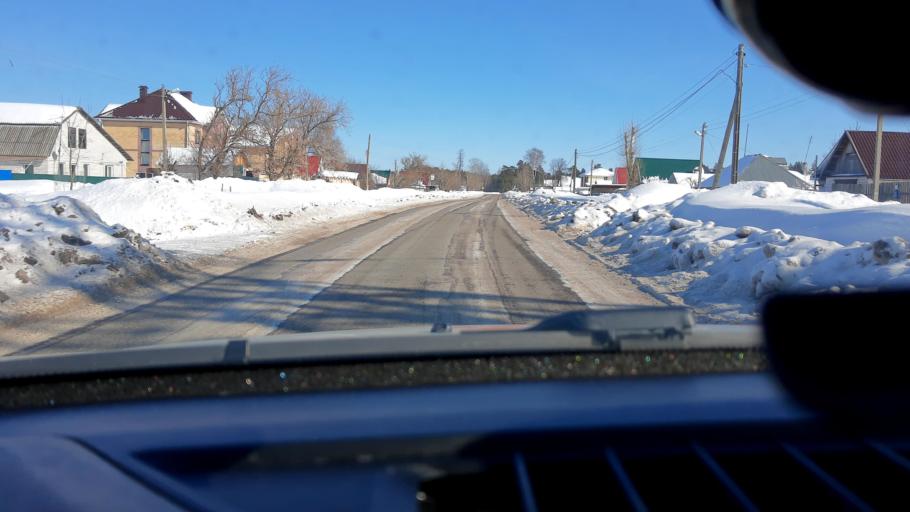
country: RU
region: Nizjnij Novgorod
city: Yuganets
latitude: 56.2323
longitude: 43.2167
